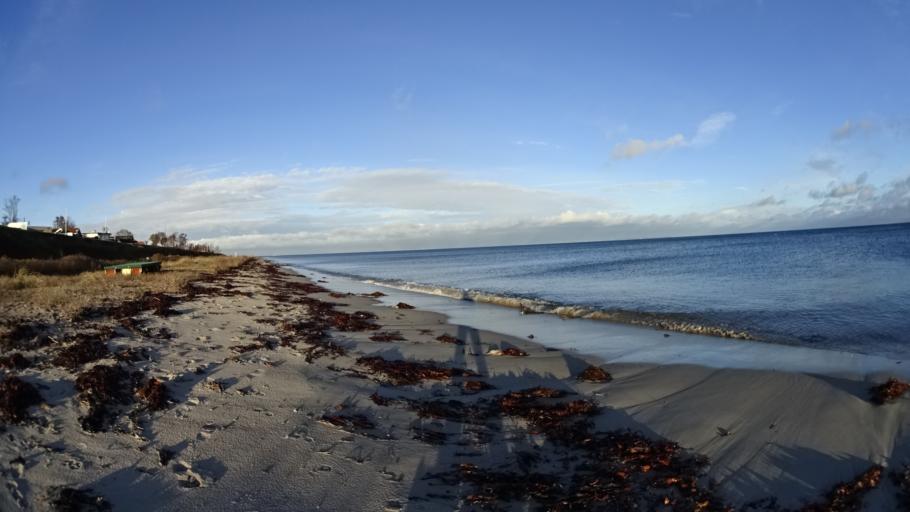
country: DK
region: Central Jutland
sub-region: Arhus Kommune
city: Beder
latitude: 56.0347
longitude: 10.2696
